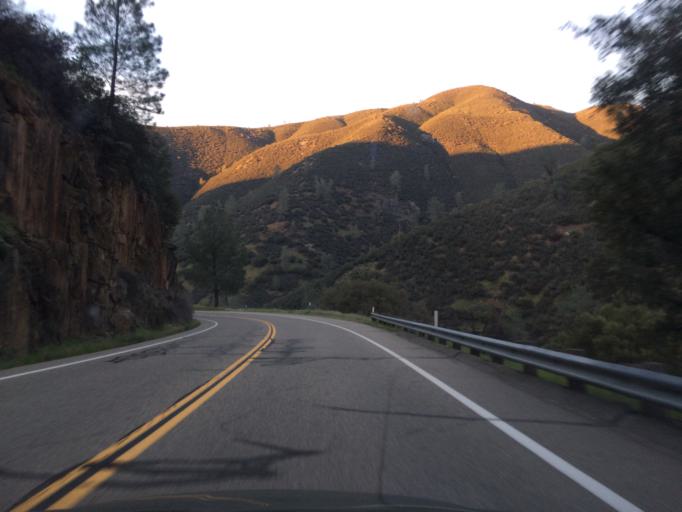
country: US
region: California
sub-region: Mariposa County
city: Midpines
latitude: 37.5956
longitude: -119.9576
